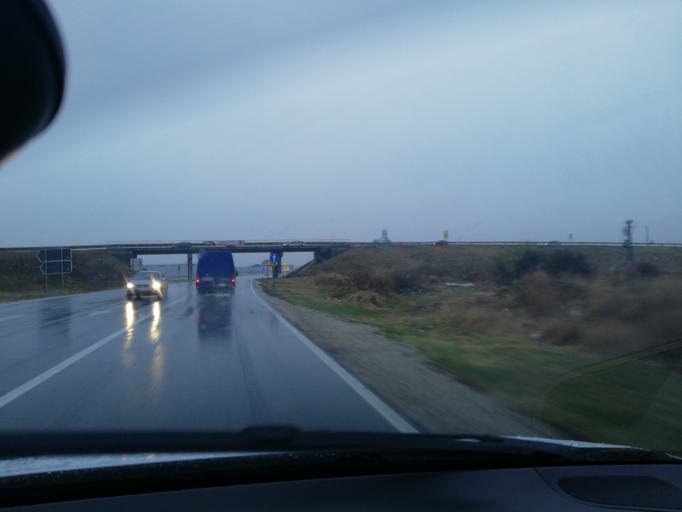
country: RS
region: Autonomna Pokrajina Vojvodina
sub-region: Sremski Okrug
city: Ruma
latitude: 45.0090
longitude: 19.8474
